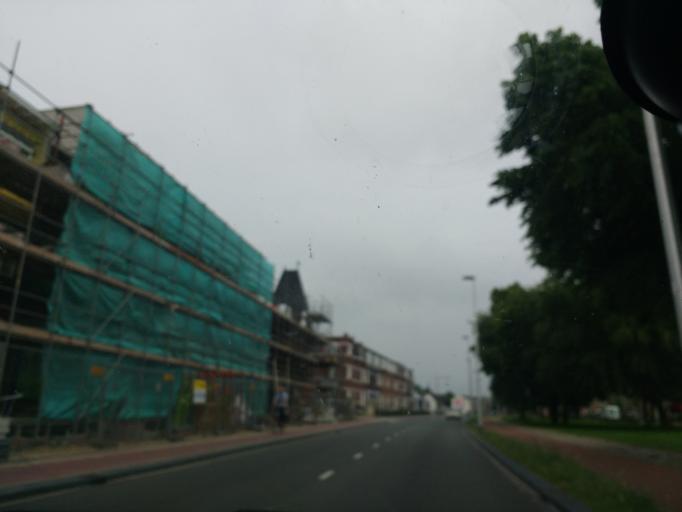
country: NL
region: Gelderland
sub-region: Gemeente Nijmegen
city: Nijmegen
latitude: 51.8534
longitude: 5.8411
